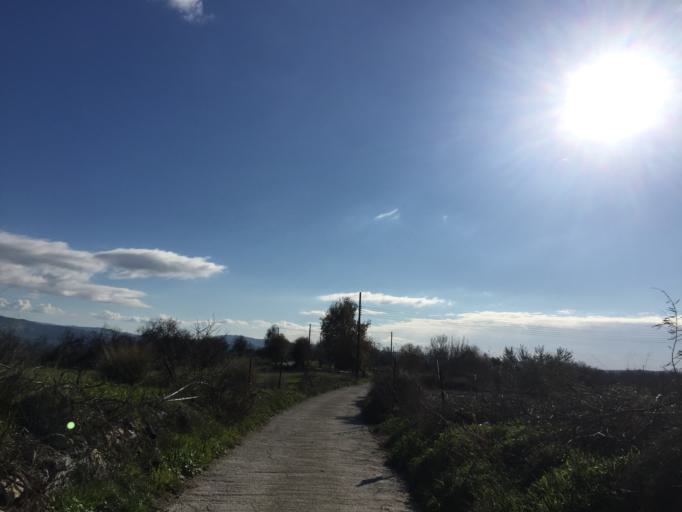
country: CY
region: Pafos
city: Mesogi
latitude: 34.8429
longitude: 32.5047
